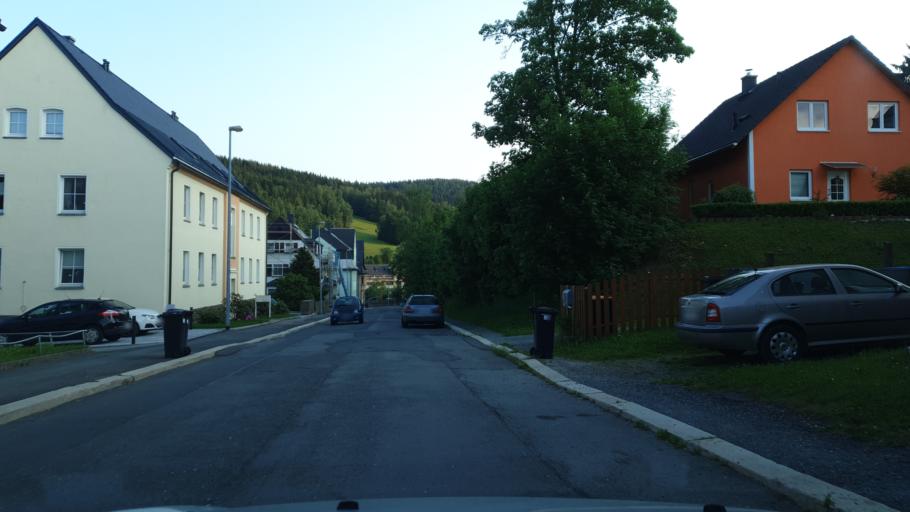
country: DE
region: Saxony
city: Klingenthal
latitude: 50.3596
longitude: 12.4602
